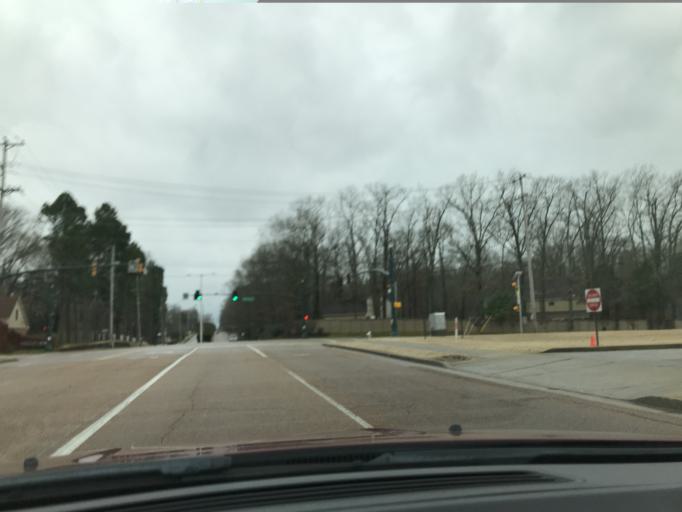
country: US
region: Tennessee
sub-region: Shelby County
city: Collierville
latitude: 35.0697
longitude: -89.6857
